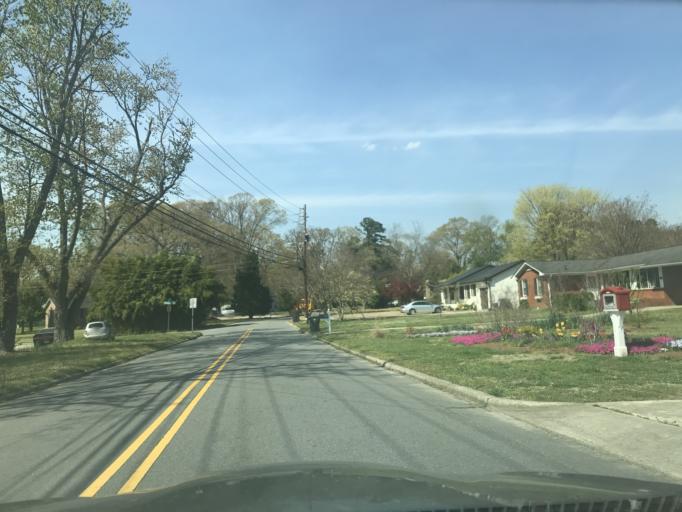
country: US
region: North Carolina
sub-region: Wake County
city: Raleigh
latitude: 35.8338
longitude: -78.6116
